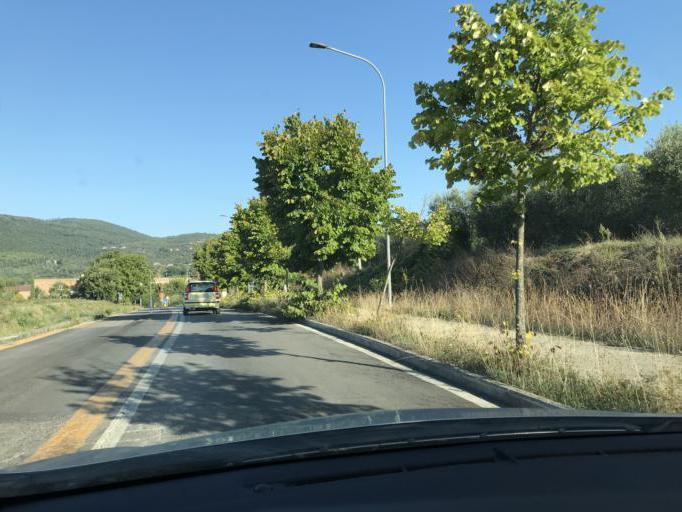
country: IT
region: Umbria
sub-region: Provincia di Perugia
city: Perugia
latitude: 43.1175
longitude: 12.3596
